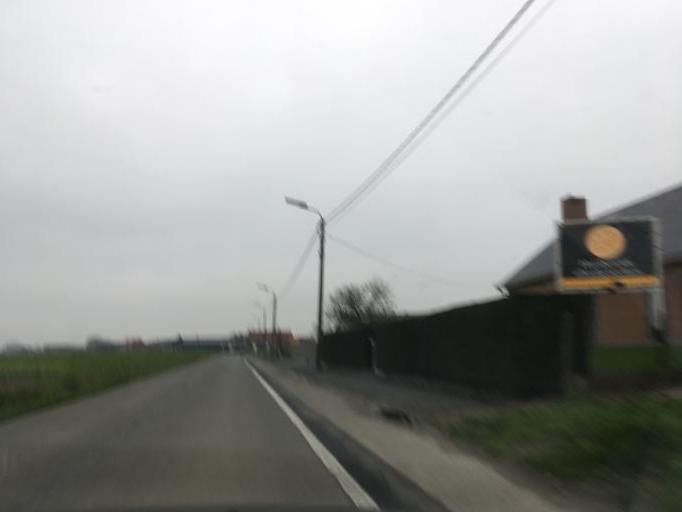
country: BE
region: Flanders
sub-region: Provincie West-Vlaanderen
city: Izegem
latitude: 50.8867
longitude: 3.1707
